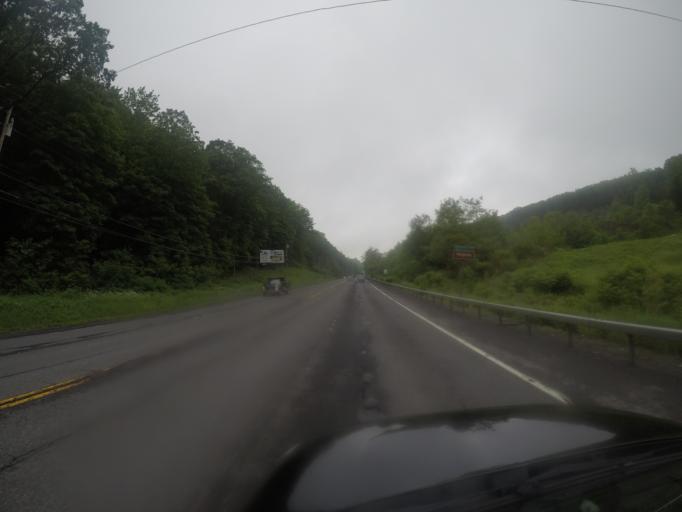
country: US
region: New York
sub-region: Ulster County
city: Hurley
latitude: 41.9643
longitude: -74.0637
